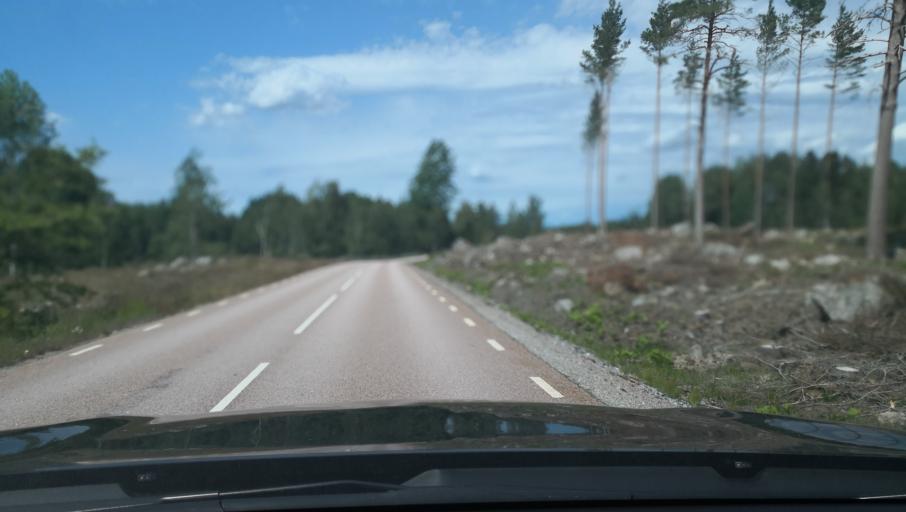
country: SE
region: Vaestmanland
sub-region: Surahammars Kommun
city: Ramnas
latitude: 59.8630
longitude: 16.0878
